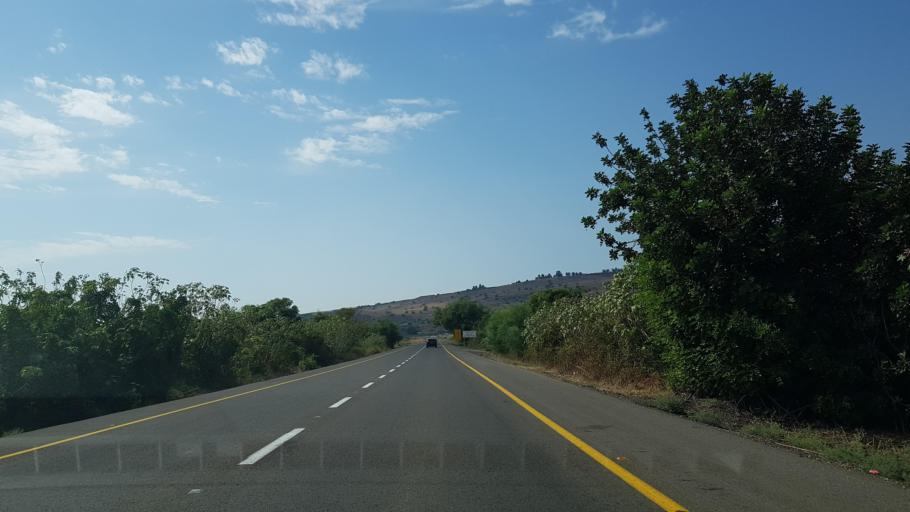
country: SY
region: Quneitra
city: Al Butayhah
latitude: 32.9042
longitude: 35.6302
